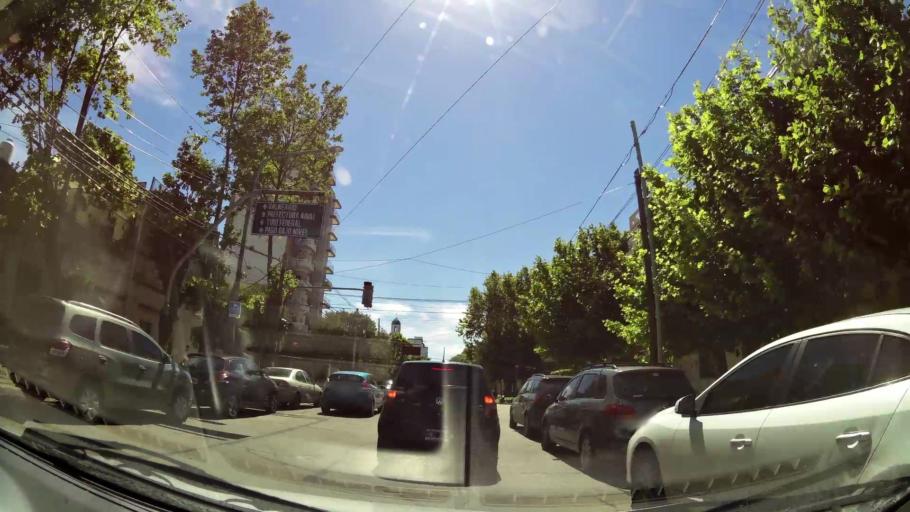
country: AR
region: Buenos Aires
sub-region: Partido de Quilmes
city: Quilmes
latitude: -34.7181
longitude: -58.2632
